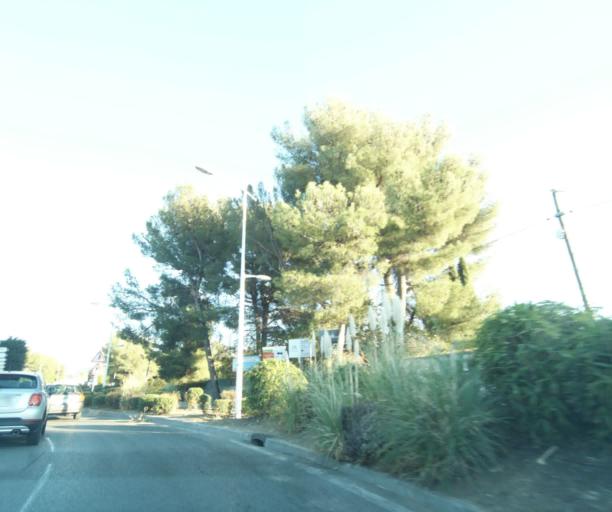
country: FR
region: Provence-Alpes-Cote d'Azur
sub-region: Departement du Var
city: Saint-Cyr-sur-Mer
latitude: 43.1832
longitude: 5.6909
